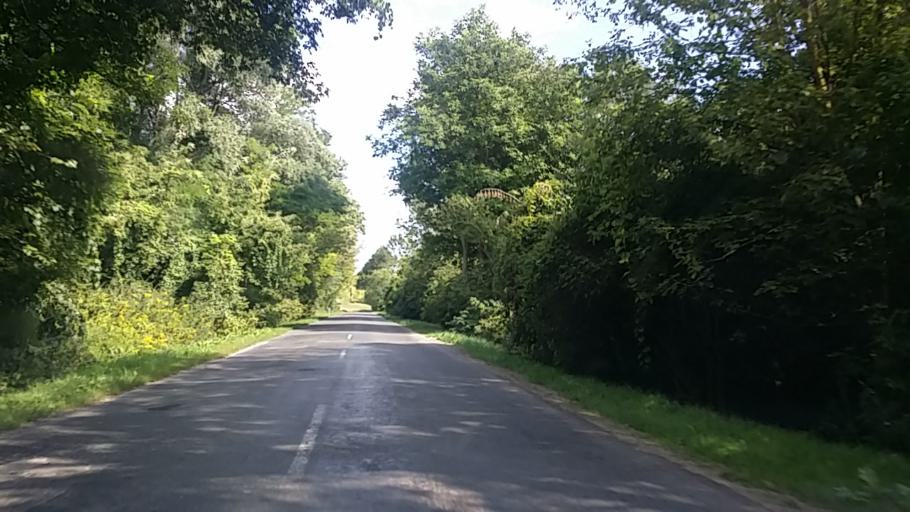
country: HU
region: Tolna
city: Gyonk
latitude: 46.5363
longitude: 18.4992
